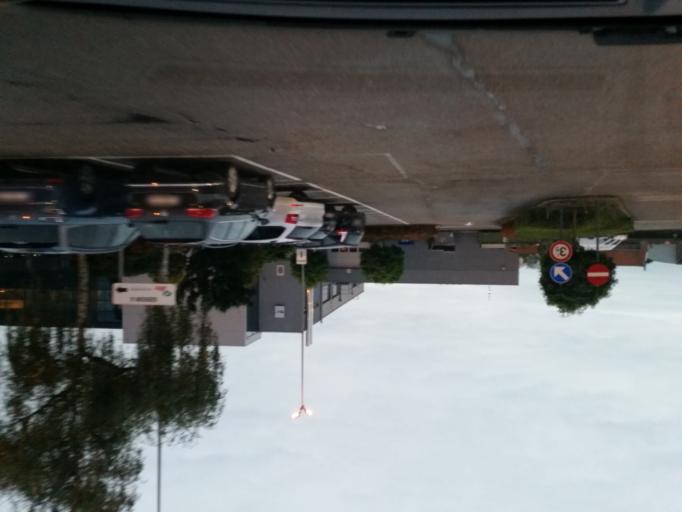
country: BE
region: Flanders
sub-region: Provincie Antwerpen
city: Mechelen
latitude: 51.0357
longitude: 4.4679
